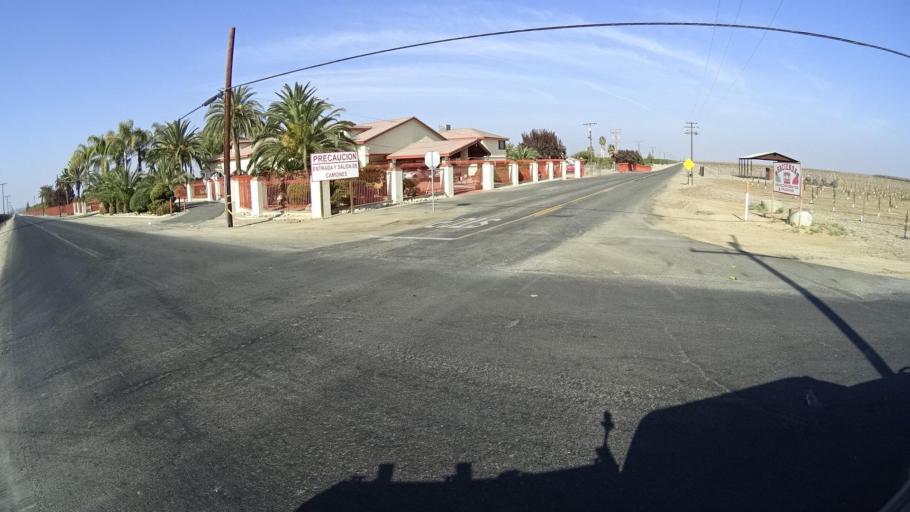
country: US
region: California
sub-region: Kern County
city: McFarland
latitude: 35.6745
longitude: -119.1693
